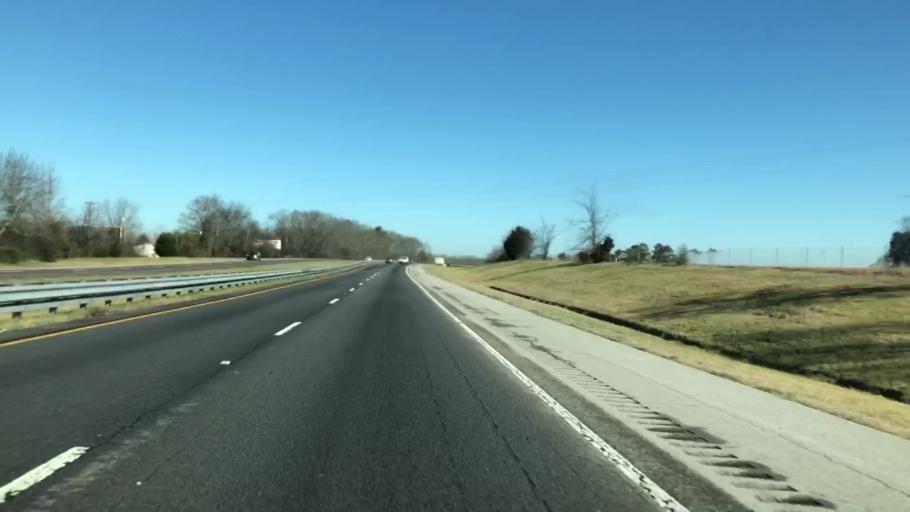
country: US
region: Alabama
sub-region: Limestone County
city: Athens
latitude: 34.8856
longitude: -86.9176
